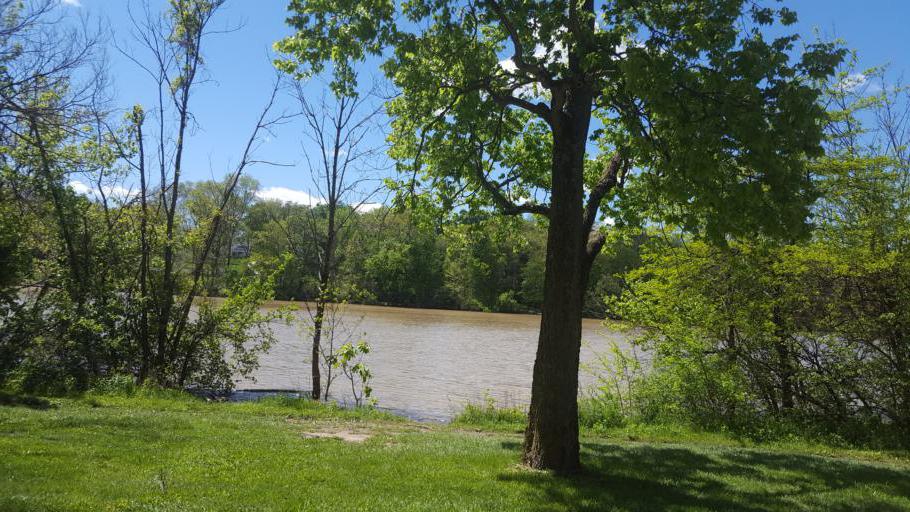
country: US
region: Ohio
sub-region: Franklin County
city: Upper Arlington
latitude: 40.0403
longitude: -83.0947
